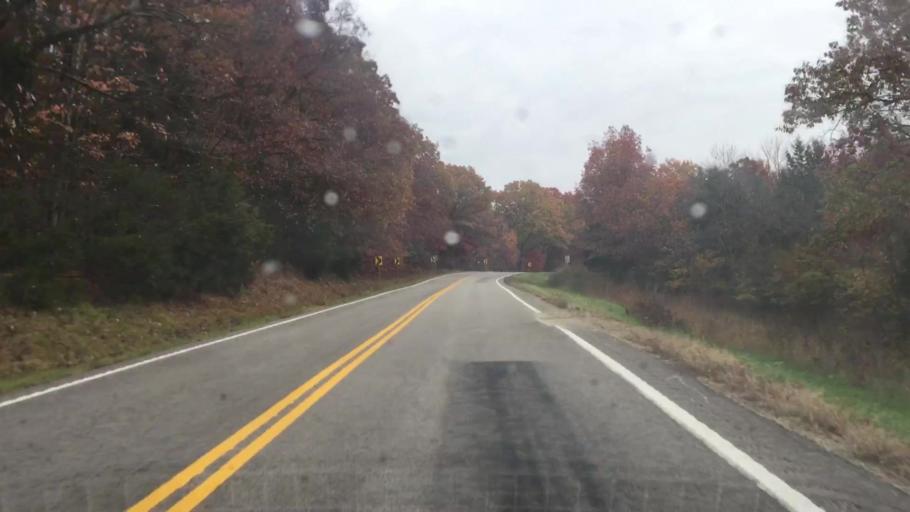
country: US
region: Missouri
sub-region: Gasconade County
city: Hermann
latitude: 38.7196
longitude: -91.6453
